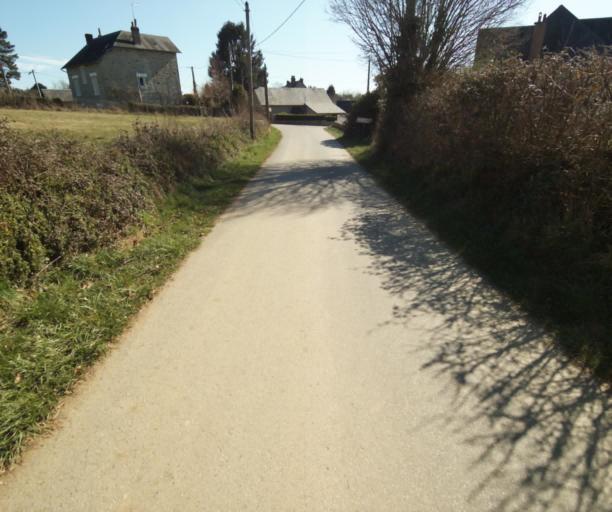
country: FR
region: Limousin
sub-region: Departement de la Correze
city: Chamboulive
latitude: 45.4715
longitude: 1.7357
